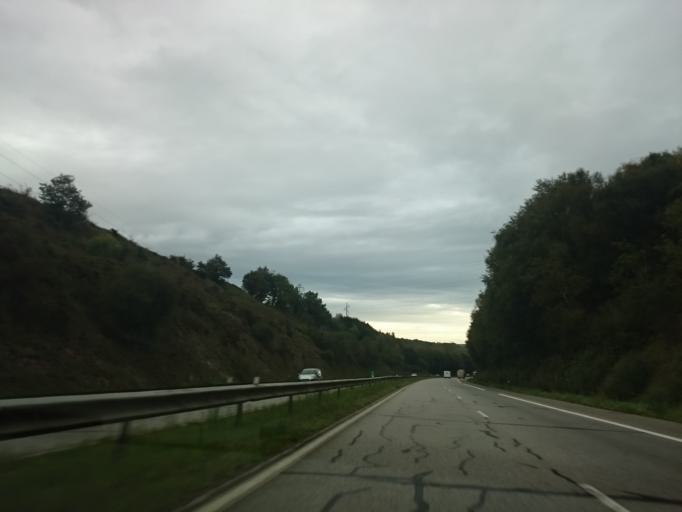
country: FR
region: Brittany
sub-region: Departement du Finistere
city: Quimper
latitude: 48.0106
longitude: -4.0693
